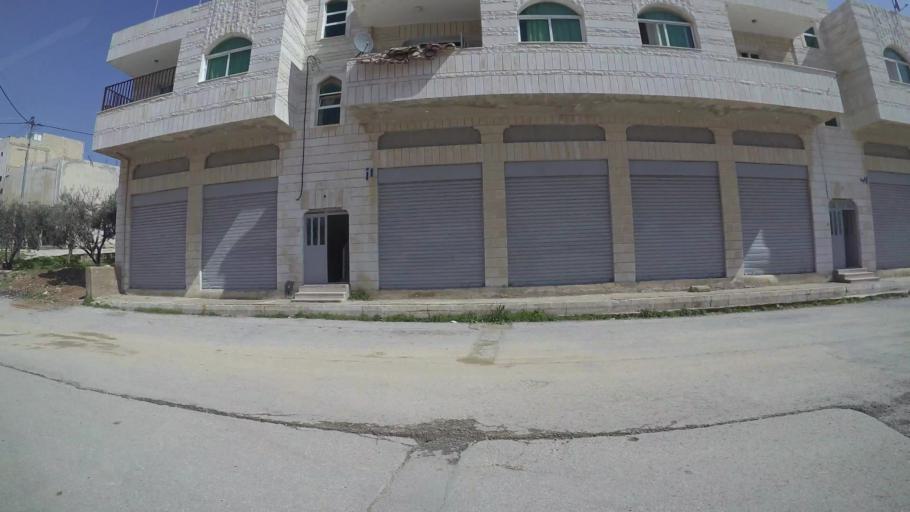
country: JO
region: Amman
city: Al Bunayyat ash Shamaliyah
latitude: 31.9014
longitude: 35.9013
